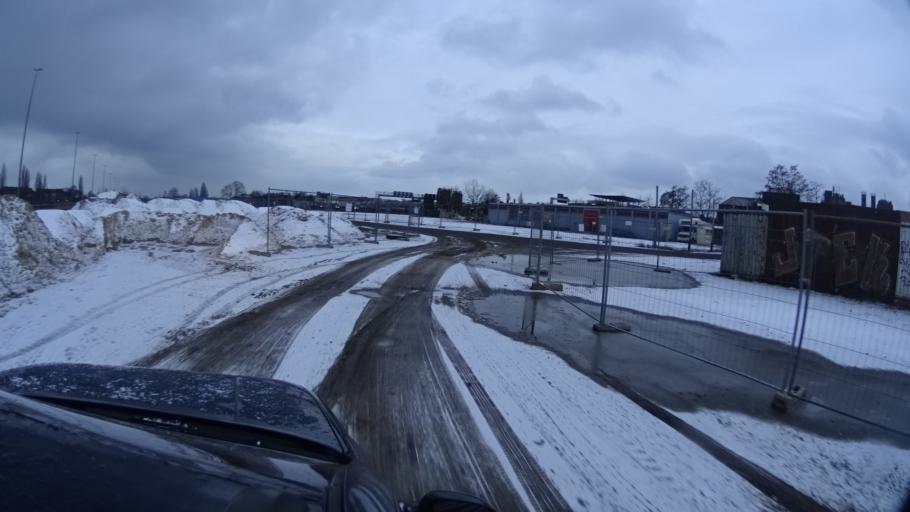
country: DE
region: Berlin
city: Tempelhof Bezirk
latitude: 52.4710
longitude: 13.3764
